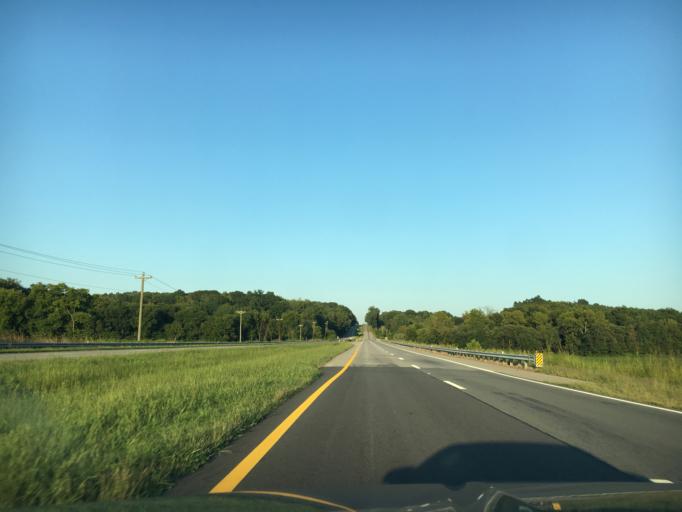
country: US
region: Virginia
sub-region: City of Danville
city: Danville
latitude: 36.5822
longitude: -79.1624
